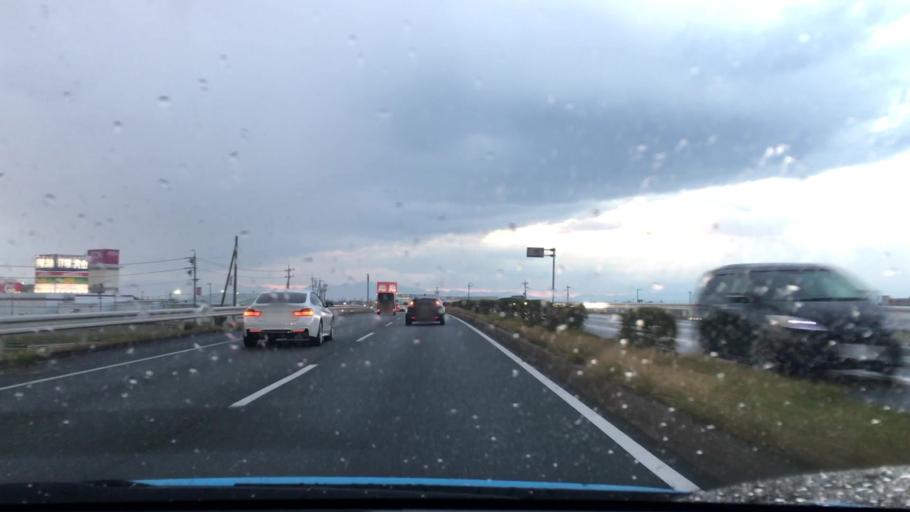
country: JP
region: Mie
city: Ise
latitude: 34.5791
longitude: 136.6216
